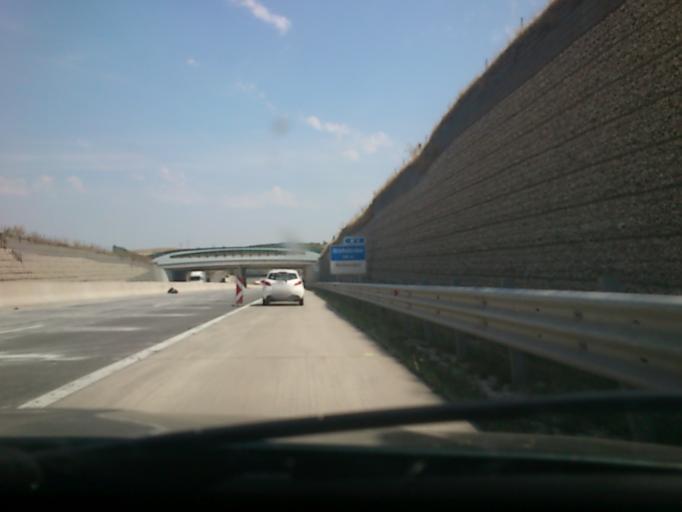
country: AT
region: Lower Austria
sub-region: Politischer Bezirk Mistelbach
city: Wolkersdorf im Weinviertel
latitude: 48.3879
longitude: 16.4971
